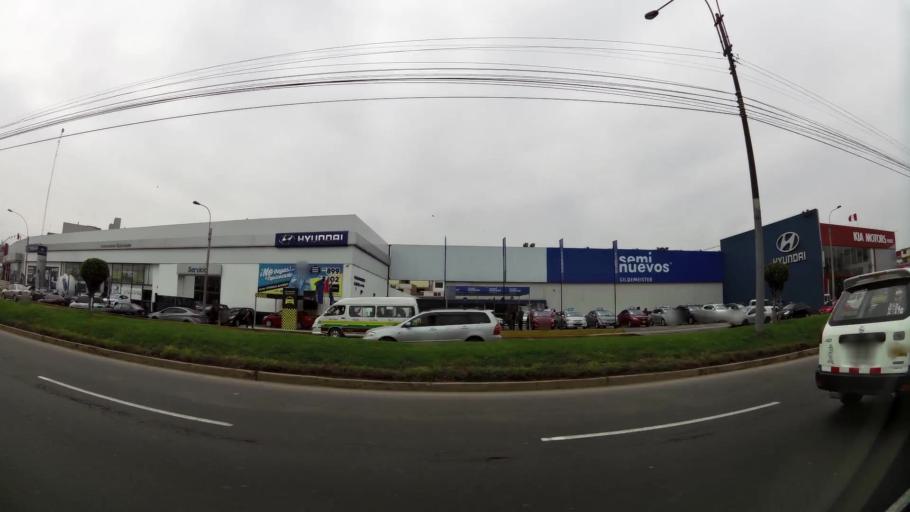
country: PE
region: Callao
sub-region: Callao
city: Callao
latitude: -12.0754
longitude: -77.0980
